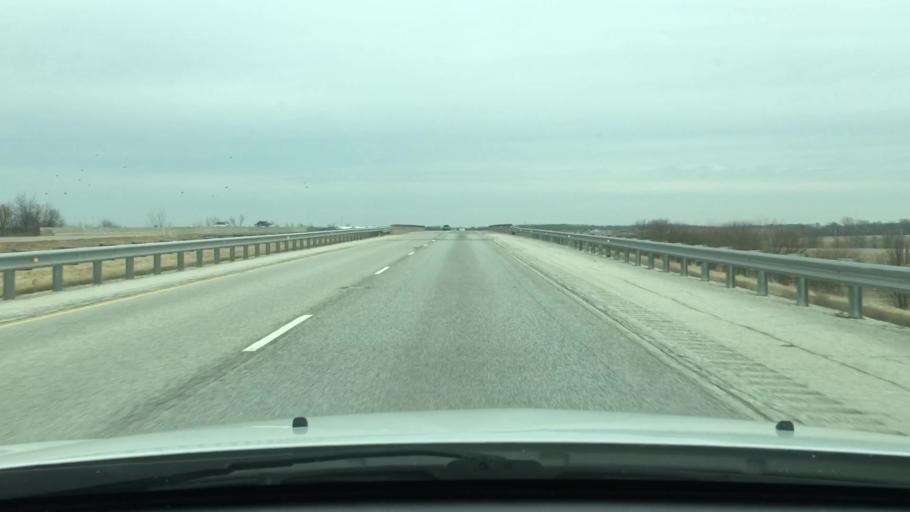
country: US
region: Illinois
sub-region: Morgan County
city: South Jacksonville
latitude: 39.7095
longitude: -90.1812
